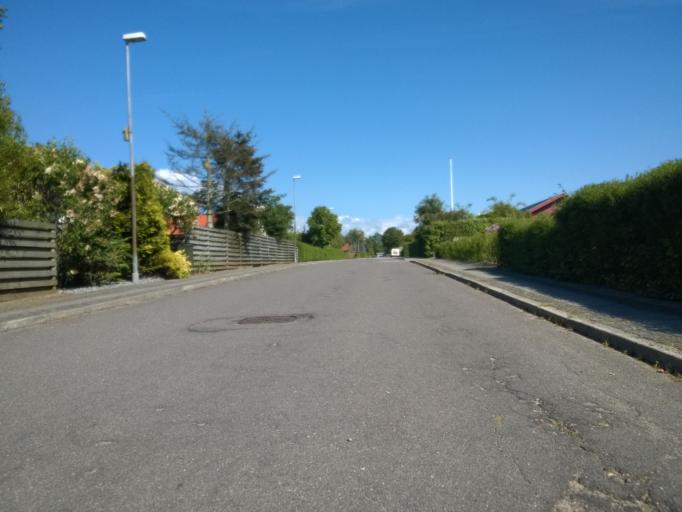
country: DK
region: Central Jutland
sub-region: Holstebro Kommune
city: Vinderup
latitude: 56.4763
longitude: 8.7716
